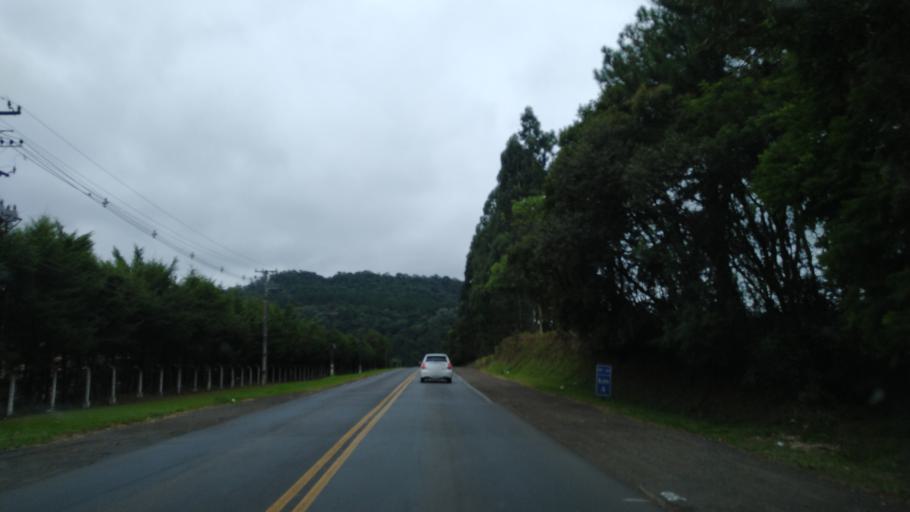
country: BR
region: Parana
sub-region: Uniao Da Vitoria
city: Uniao da Vitoria
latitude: -26.2342
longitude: -51.1262
